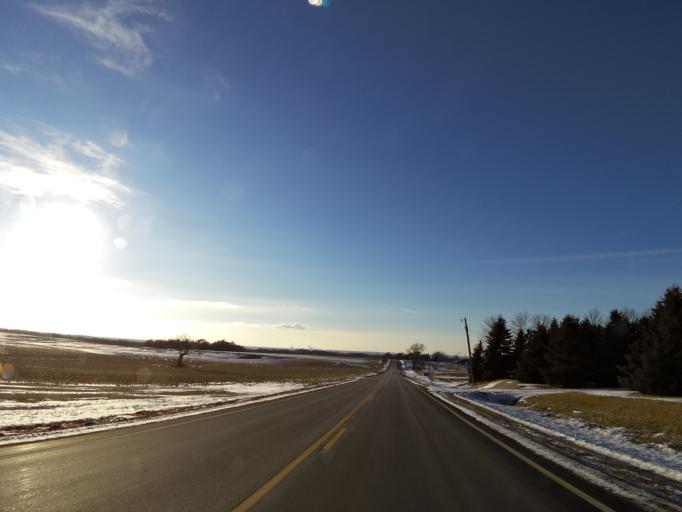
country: US
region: Minnesota
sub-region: Dakota County
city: Hastings
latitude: 44.7902
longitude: -92.8517
